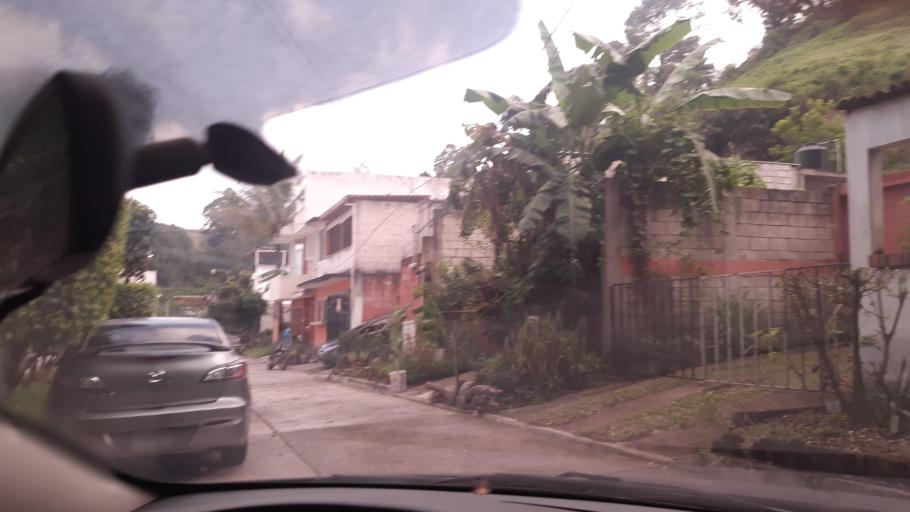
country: GT
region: Guatemala
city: Petapa
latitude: 14.5070
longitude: -90.5427
